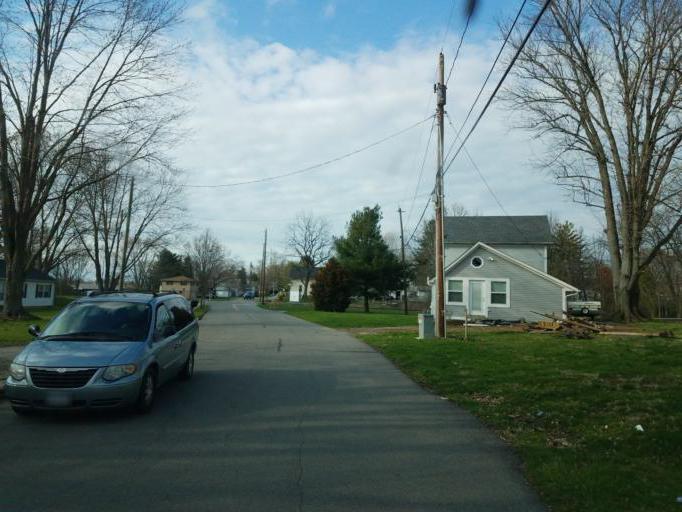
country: US
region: Ohio
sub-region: Delaware County
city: Delaware
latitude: 40.2951
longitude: -83.0555
